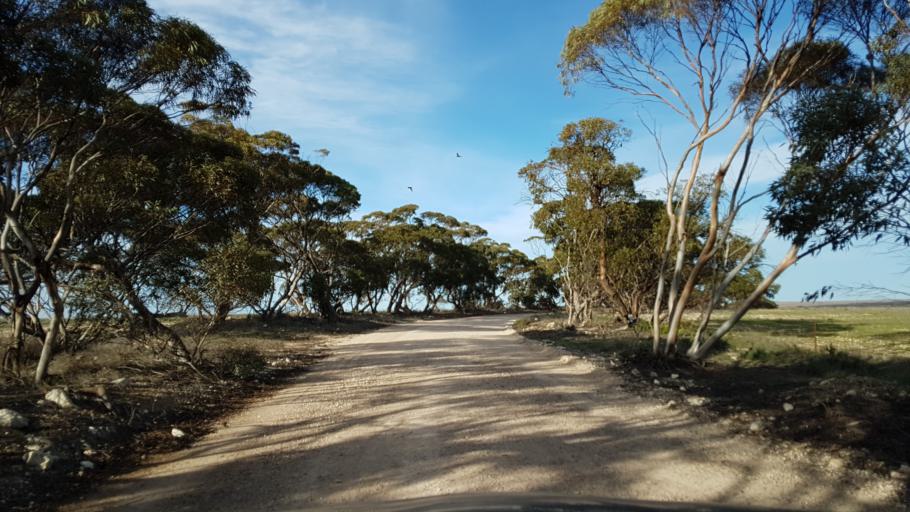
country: AU
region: South Australia
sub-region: Mid Murray
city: Mannum
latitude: -34.9768
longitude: 139.5763
